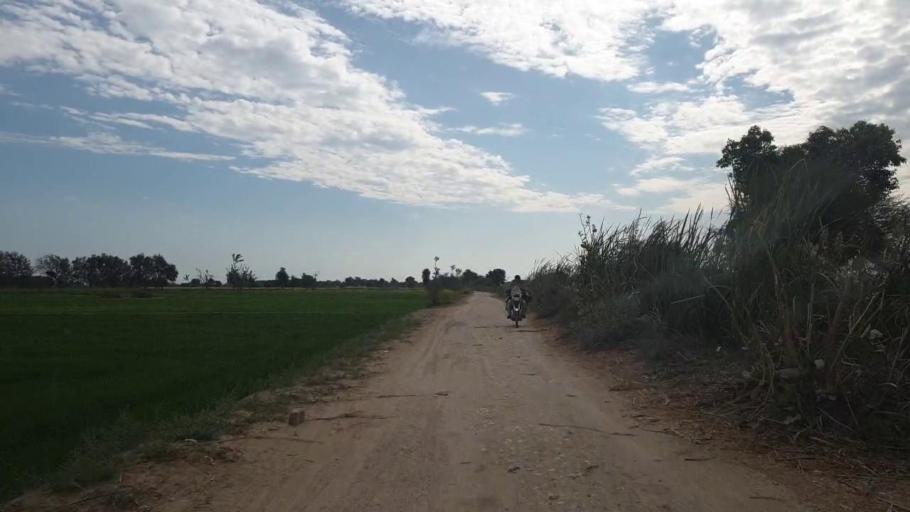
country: PK
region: Sindh
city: Jhol
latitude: 25.9908
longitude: 68.8986
